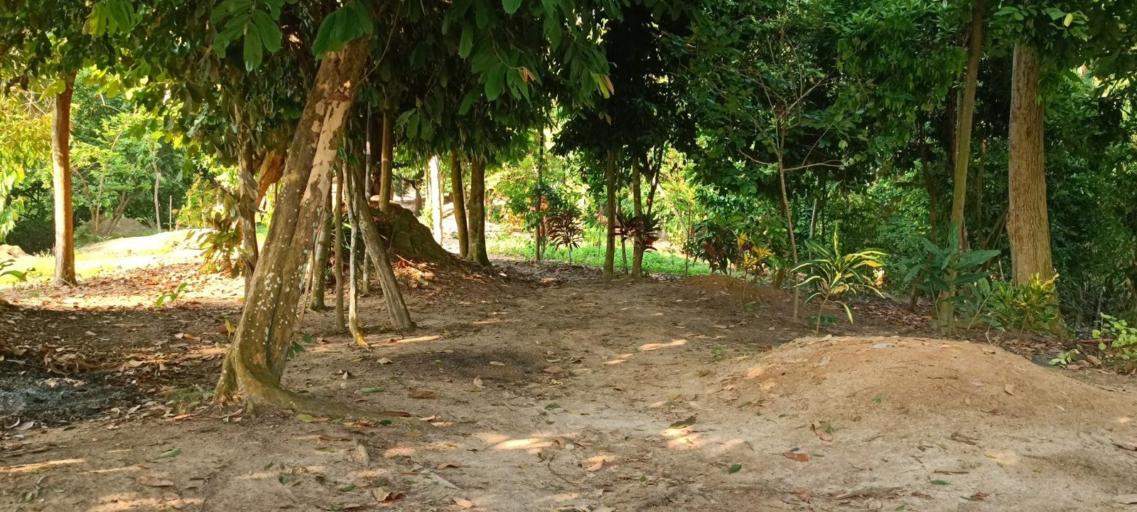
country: MY
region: Penang
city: Juru
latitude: 5.3352
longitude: 100.4121
